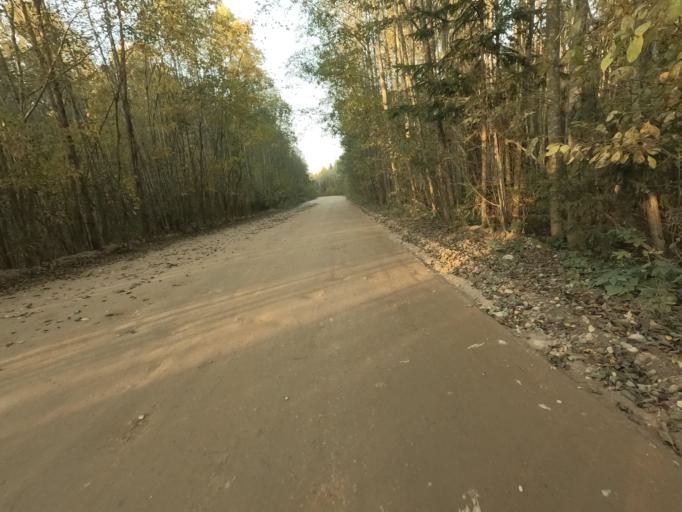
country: RU
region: Leningrad
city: Lyuban'
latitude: 58.9921
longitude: 31.1051
